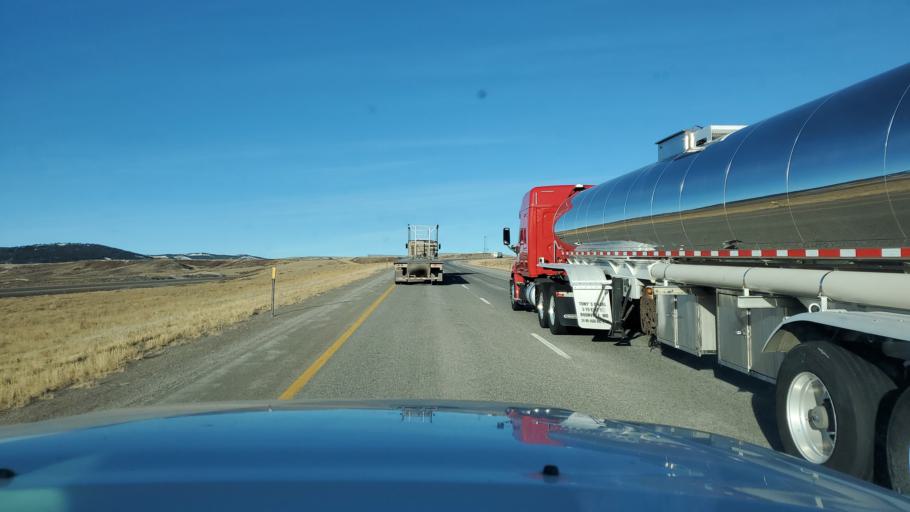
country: US
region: Wyoming
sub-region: Albany County
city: Laramie
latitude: 41.5271
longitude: -106.0636
